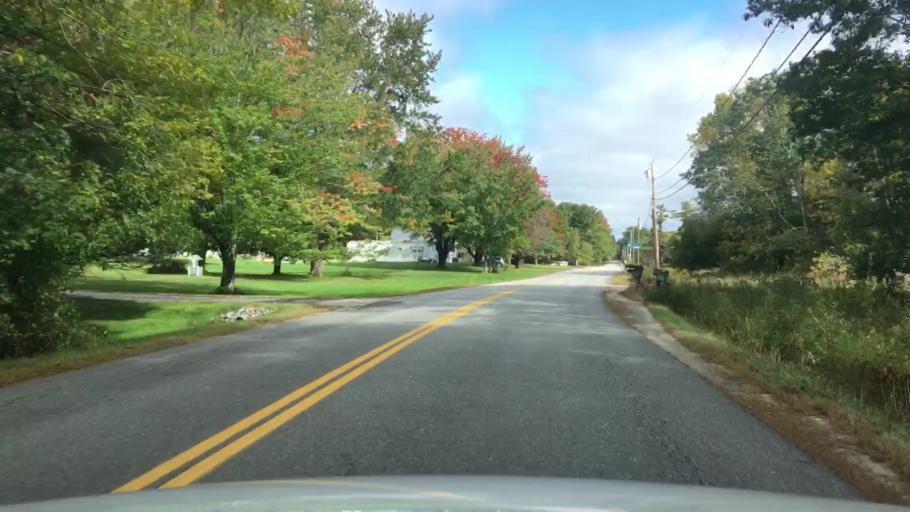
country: US
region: Maine
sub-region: Cumberland County
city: Brunswick
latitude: 43.9353
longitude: -69.9062
